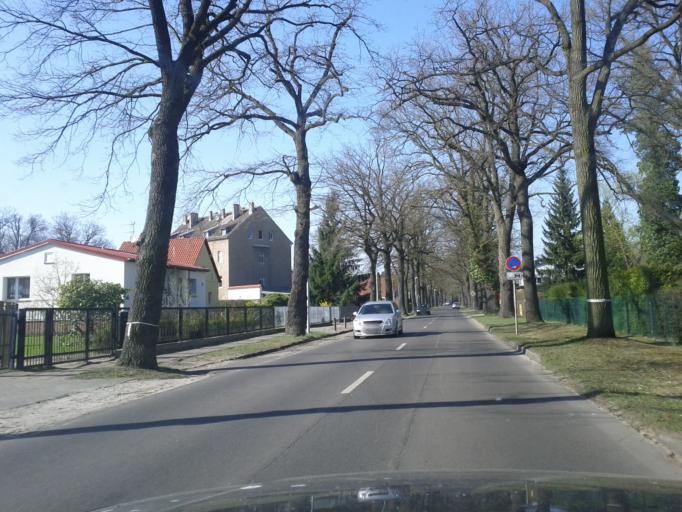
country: DE
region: Brandenburg
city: Schoneiche
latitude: 52.4681
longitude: 13.6954
